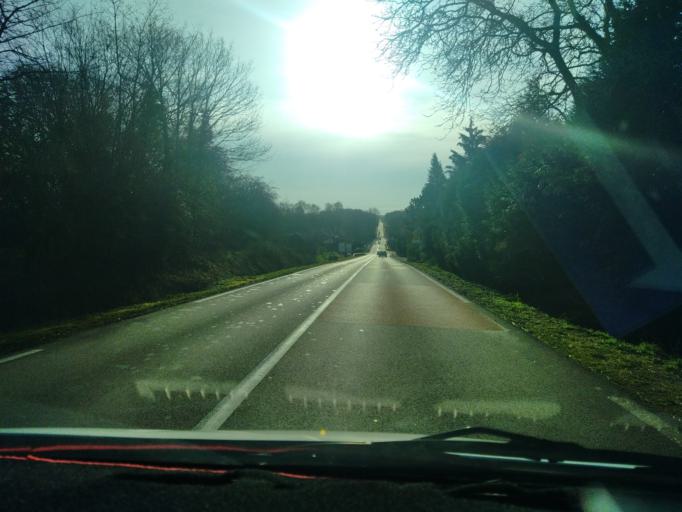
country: FR
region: Franche-Comte
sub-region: Departement de la Haute-Saone
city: Gray
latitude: 47.3939
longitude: 5.6506
